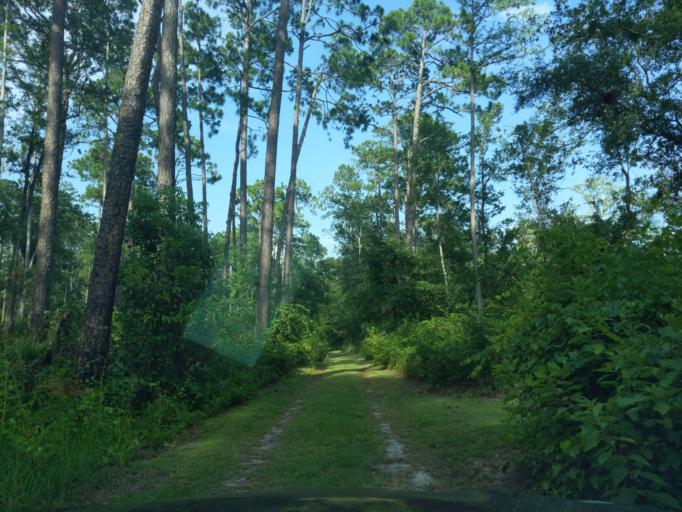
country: US
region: Florida
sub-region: Gadsden County
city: Midway
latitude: 30.4057
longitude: -84.4057
